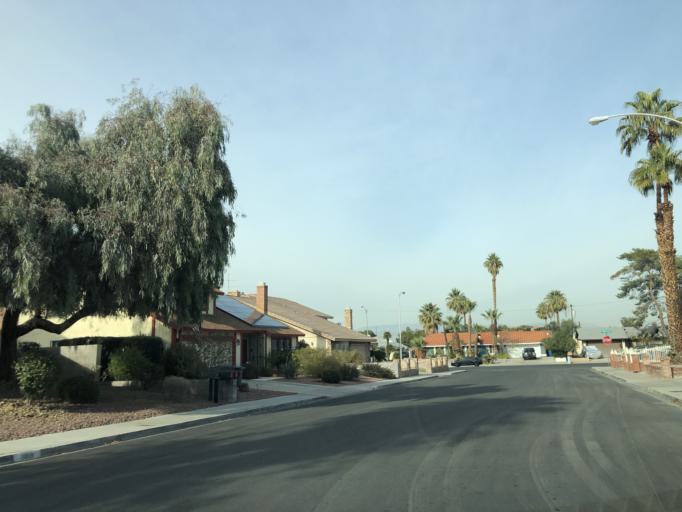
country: US
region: Nevada
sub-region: Clark County
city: Winchester
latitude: 36.1176
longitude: -115.1268
